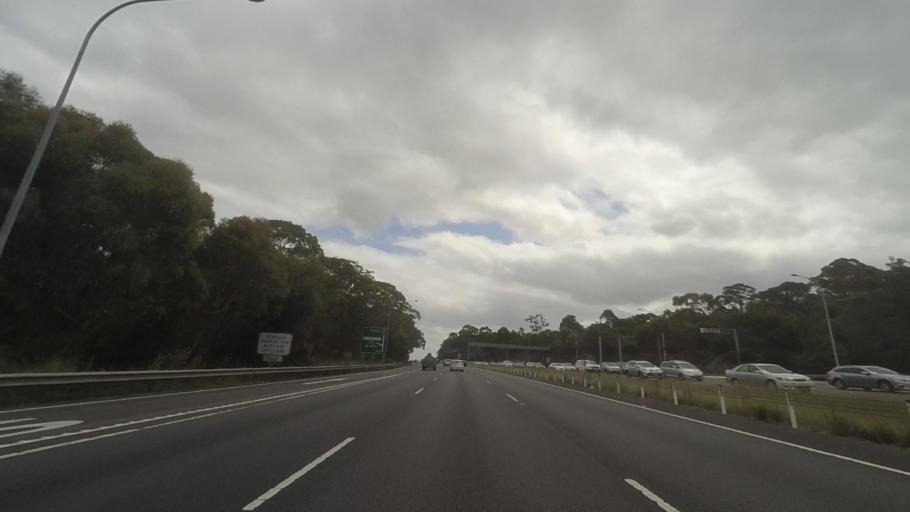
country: AU
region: New South Wales
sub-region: Gosford Shire
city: Point Clare
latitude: -33.4546
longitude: 151.2066
